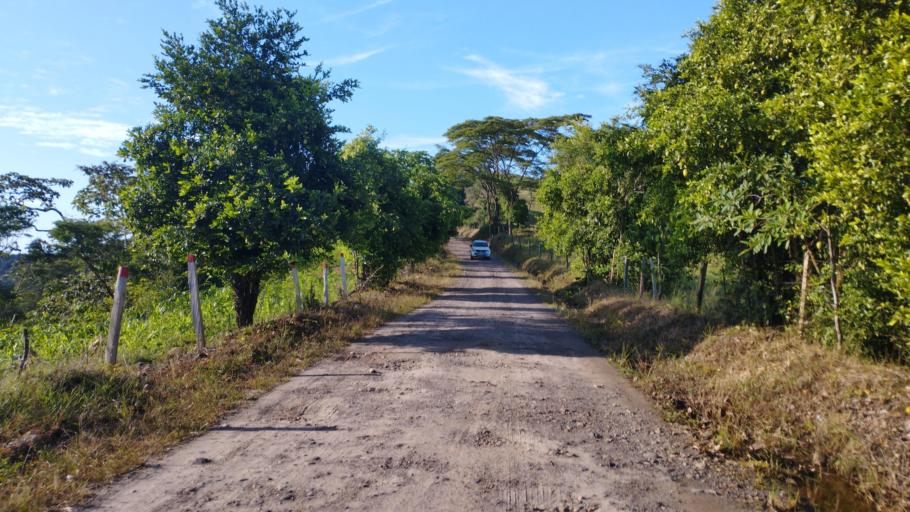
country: CO
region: Casanare
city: Sabanalarga
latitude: 4.7965
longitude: -73.0929
